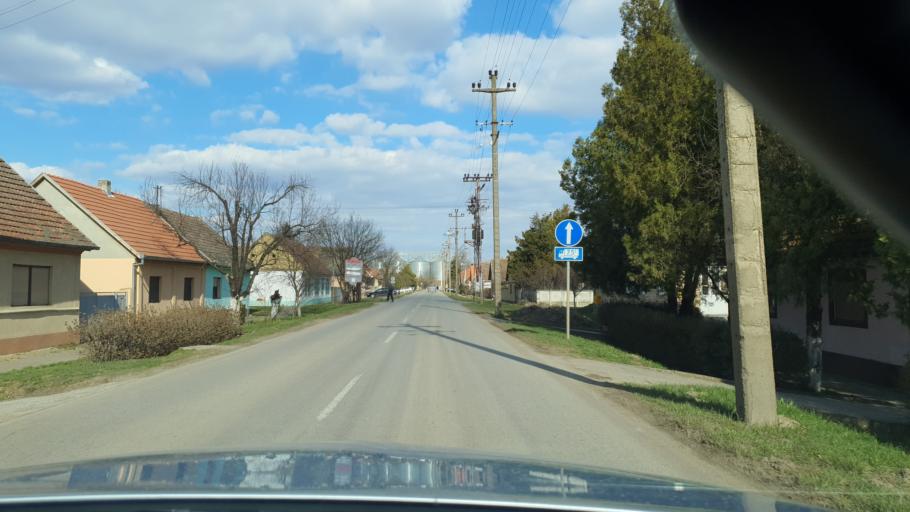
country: RS
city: Ravno Selo
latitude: 45.4503
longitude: 19.6295
